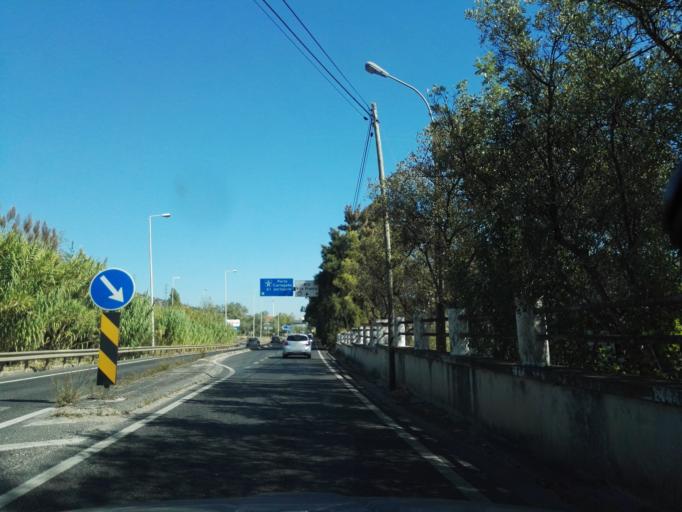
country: PT
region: Lisbon
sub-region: Vila Franca de Xira
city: Alhandra
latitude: 38.9368
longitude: -9.0027
